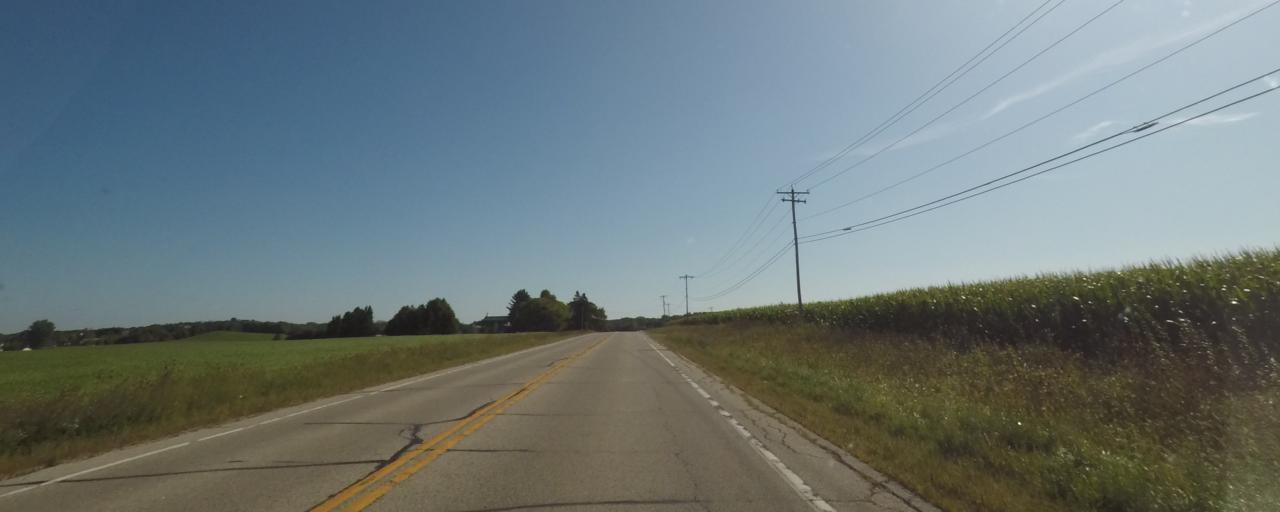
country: US
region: Wisconsin
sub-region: Waukesha County
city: Dousman
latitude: 43.0218
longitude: -88.5510
